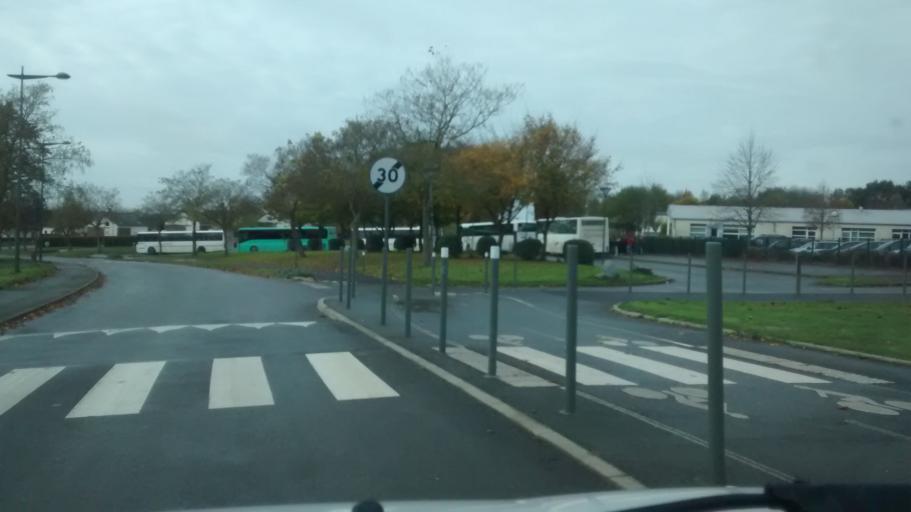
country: FR
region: Brittany
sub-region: Departement d'Ille-et-Vilaine
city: Chateaubourg
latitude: 48.1141
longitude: -1.3847
